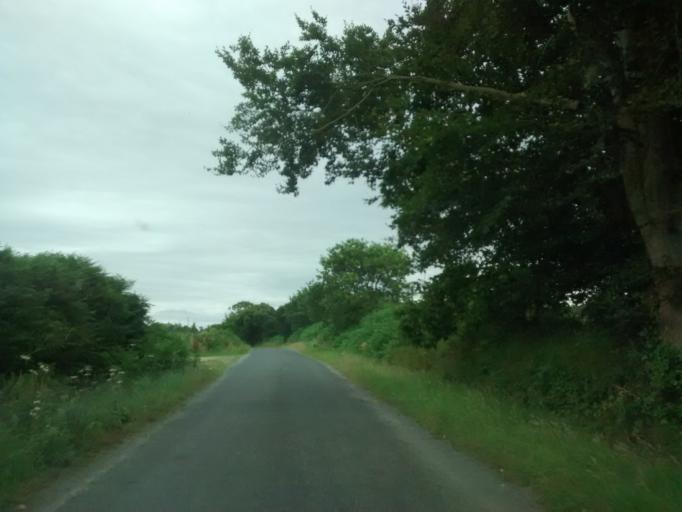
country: FR
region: Brittany
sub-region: Departement des Cotes-d'Armor
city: Trelevern
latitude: 48.7861
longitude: -3.3518
